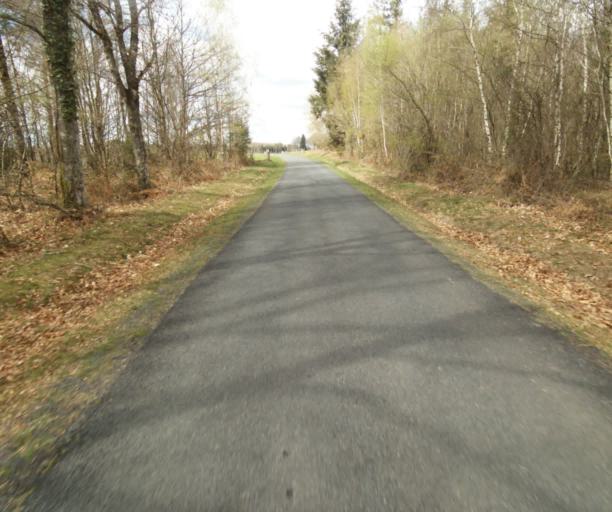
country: FR
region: Limousin
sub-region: Departement de la Correze
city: Argentat
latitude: 45.1994
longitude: 1.9082
